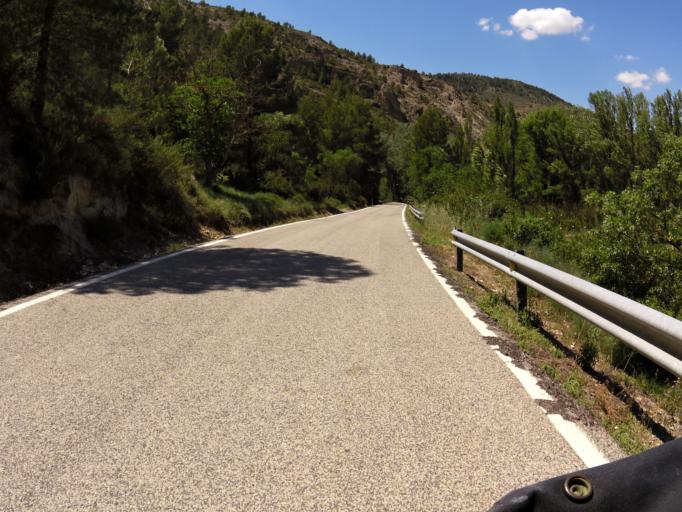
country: ES
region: Valencia
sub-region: Provincia de Valencia
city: Casas Bajas
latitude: 40.0006
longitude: -1.2753
